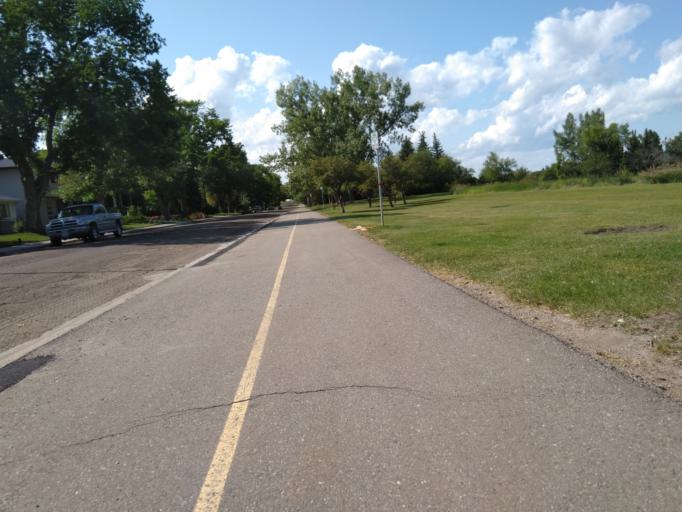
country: CA
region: Alberta
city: Calgary
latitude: 51.0793
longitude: -114.1108
